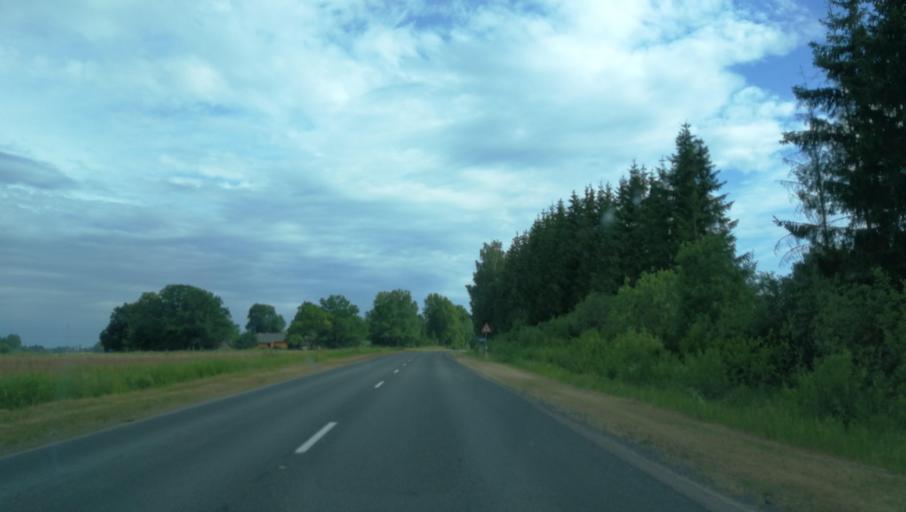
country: LV
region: Valmieras Rajons
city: Valmiera
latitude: 57.5962
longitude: 25.4601
